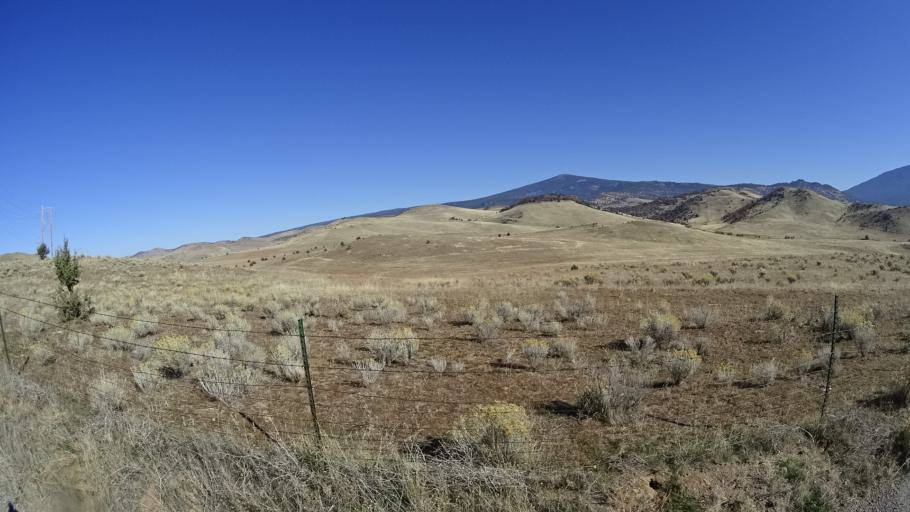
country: US
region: California
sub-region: Siskiyou County
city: Montague
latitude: 41.7692
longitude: -122.3588
